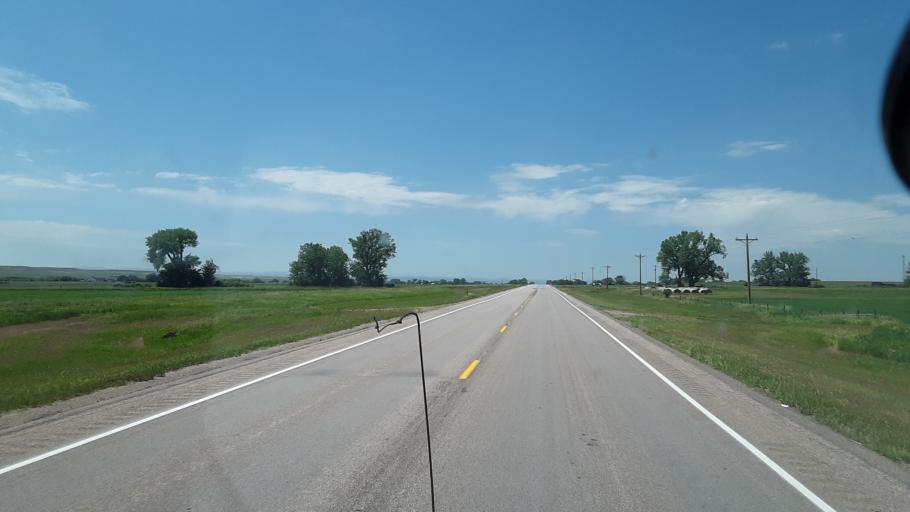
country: US
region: South Dakota
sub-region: Pennington County
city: Box Elder
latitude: 43.9849
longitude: -102.9564
